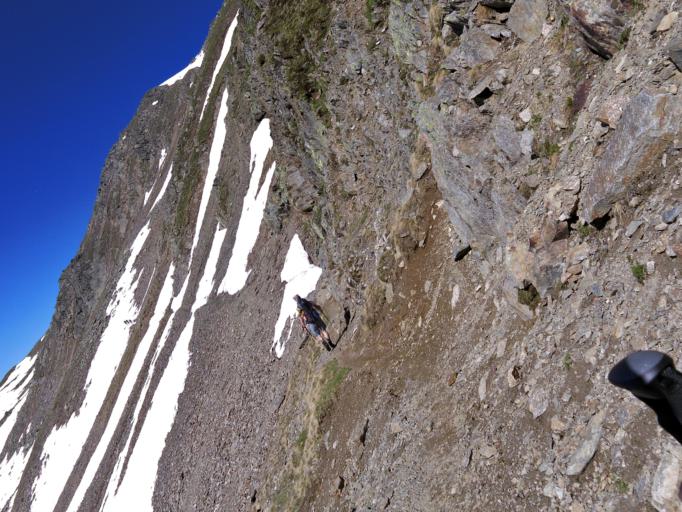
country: AT
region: Tyrol
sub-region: Politischer Bezirk Innsbruck Land
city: Neustift im Stubaital
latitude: 47.1431
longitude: 11.2636
